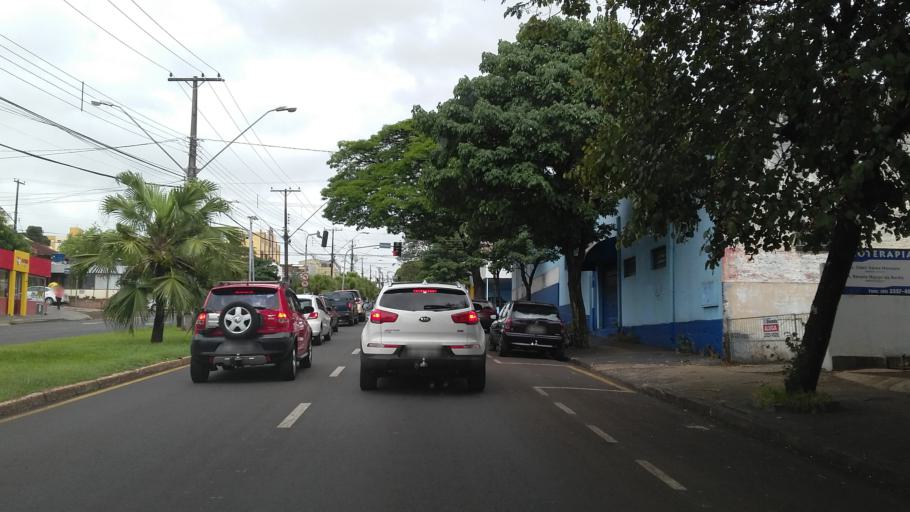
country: BR
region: Parana
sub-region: Londrina
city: Londrina
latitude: -23.3198
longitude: -51.1519
